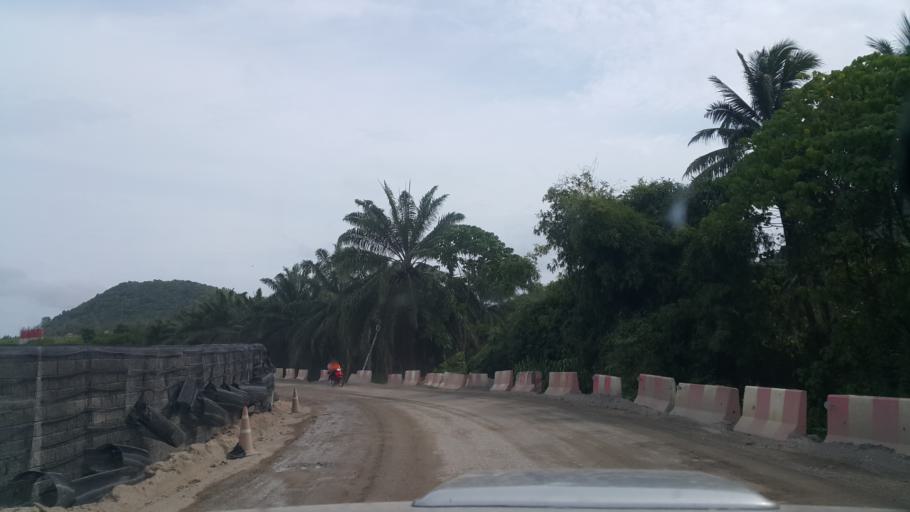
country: TH
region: Rayong
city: Ban Chang
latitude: 12.7673
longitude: 100.9939
